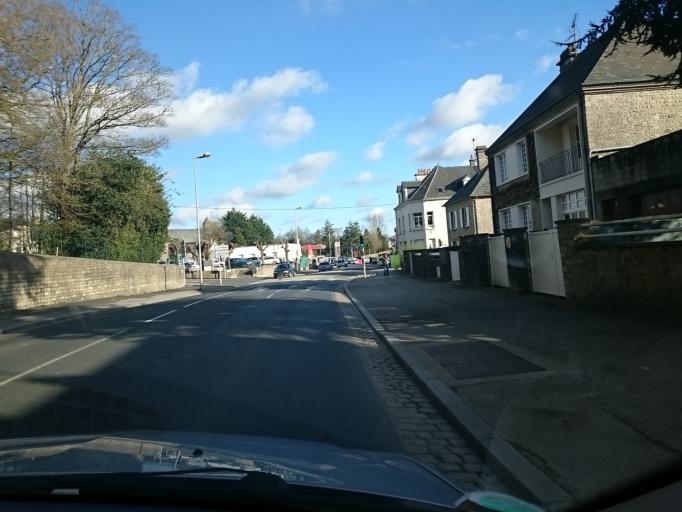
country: FR
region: Lower Normandy
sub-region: Departement de la Manche
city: Valognes
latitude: 49.5084
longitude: -1.4673
